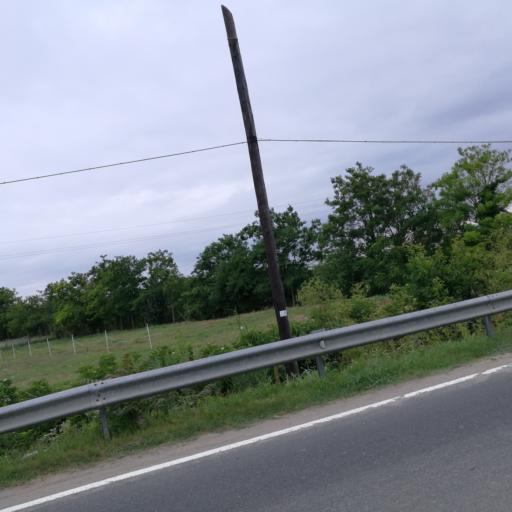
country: RO
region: Constanta
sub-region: Municipiul Mangalia
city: Mangalia
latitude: 43.7548
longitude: 28.5718
